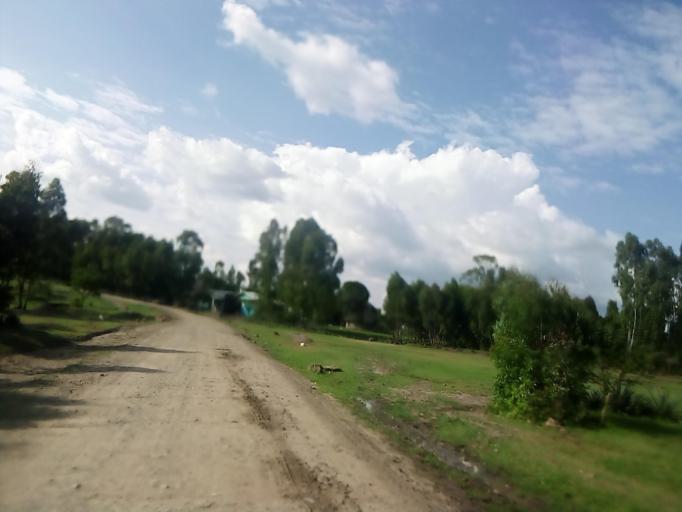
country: ET
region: Southern Nations, Nationalities, and People's Region
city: K'olito
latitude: 7.6391
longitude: 38.0590
